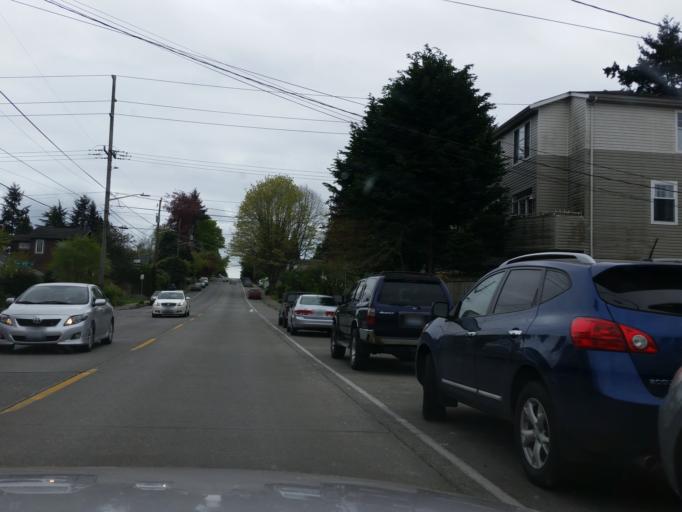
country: US
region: Washington
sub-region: King County
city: Shoreline
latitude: 47.6984
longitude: -122.3661
